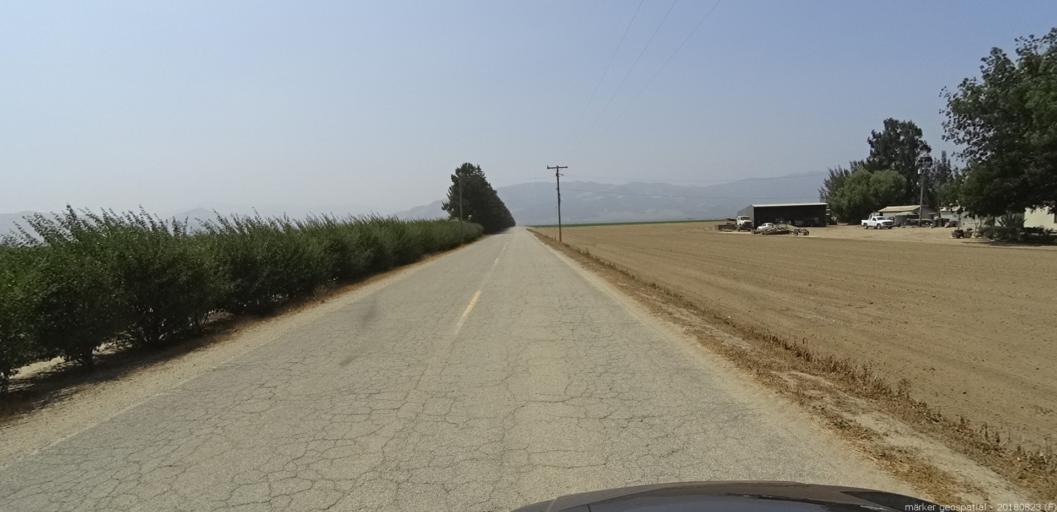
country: US
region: California
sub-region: Monterey County
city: Greenfield
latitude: 36.3361
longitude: -121.2626
